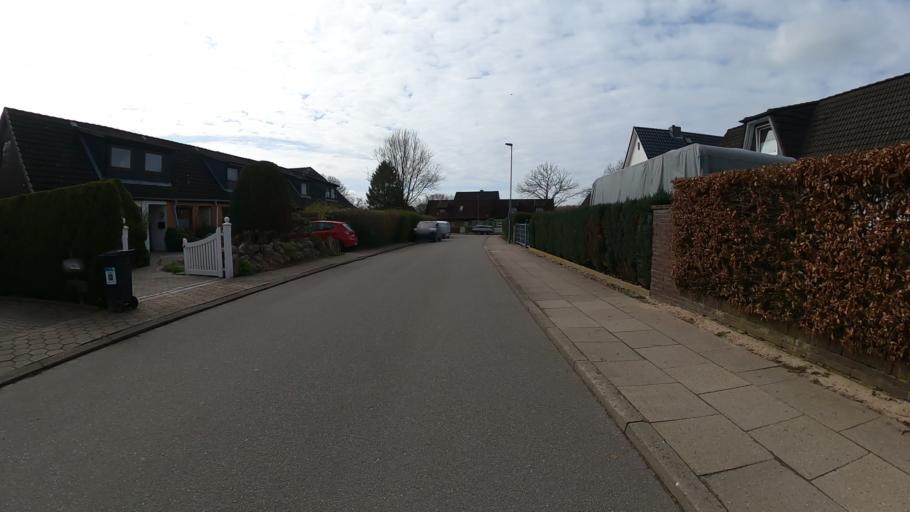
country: DE
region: Schleswig-Holstein
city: Ahrensburg
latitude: 53.6393
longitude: 10.2166
